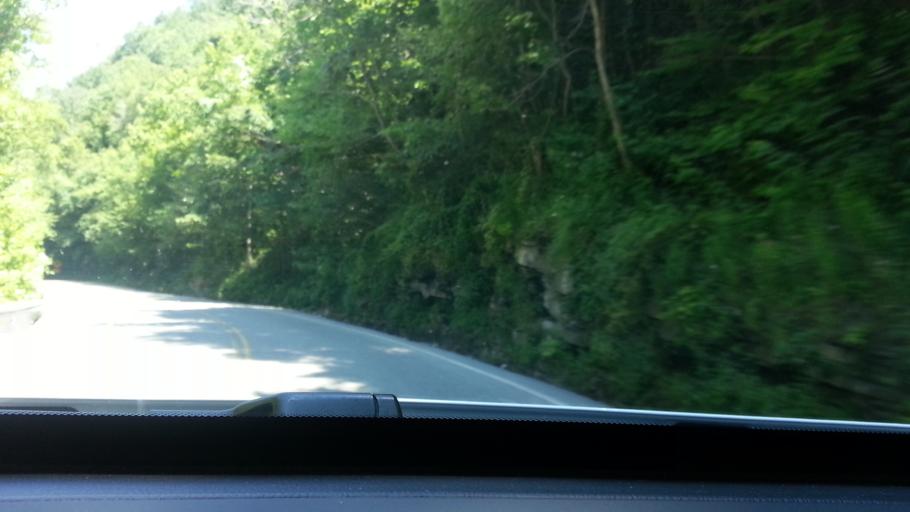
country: US
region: West Virginia
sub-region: Fayette County
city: Ansted
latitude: 38.1086
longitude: -81.1469
